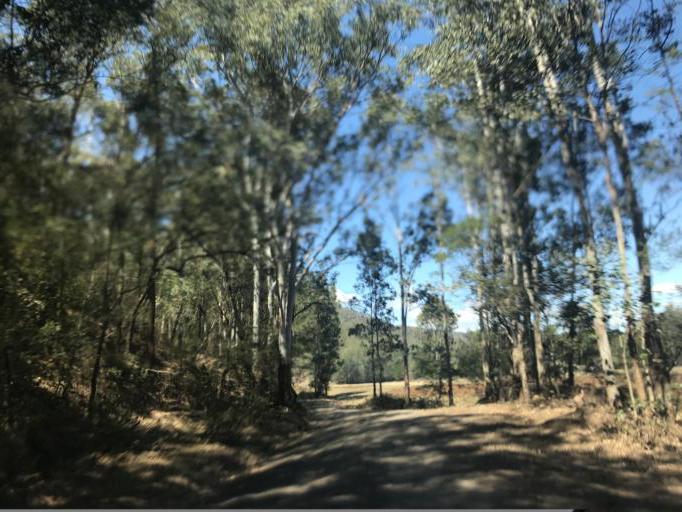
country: AU
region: New South Wales
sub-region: Hornsby Shire
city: Glenorie
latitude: -33.2172
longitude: 150.9782
